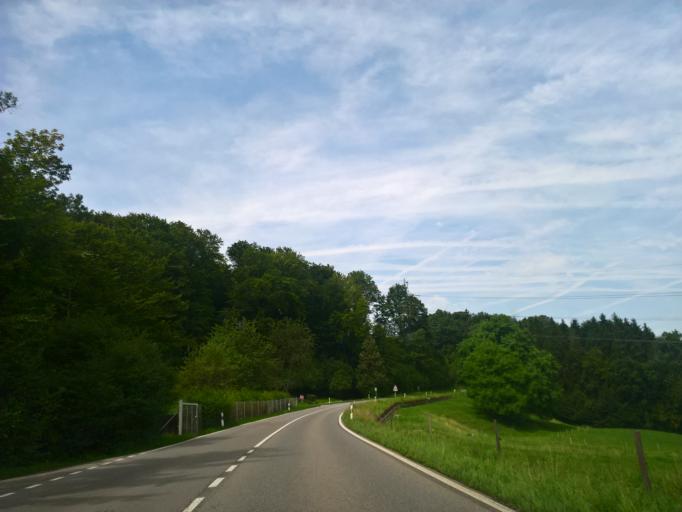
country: CH
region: Zurich
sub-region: Bezirk Buelach
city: Buelach / Soligaenter
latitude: 47.5462
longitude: 8.5527
